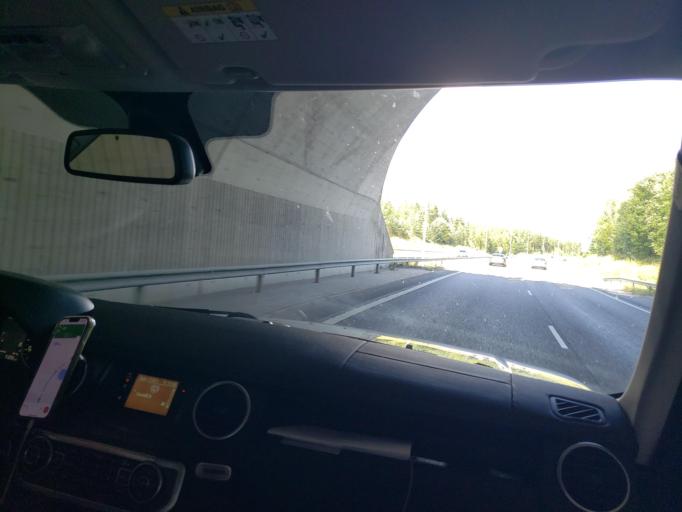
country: FI
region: Uusimaa
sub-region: Helsinki
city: Lohja
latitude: 60.3004
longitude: 24.1895
